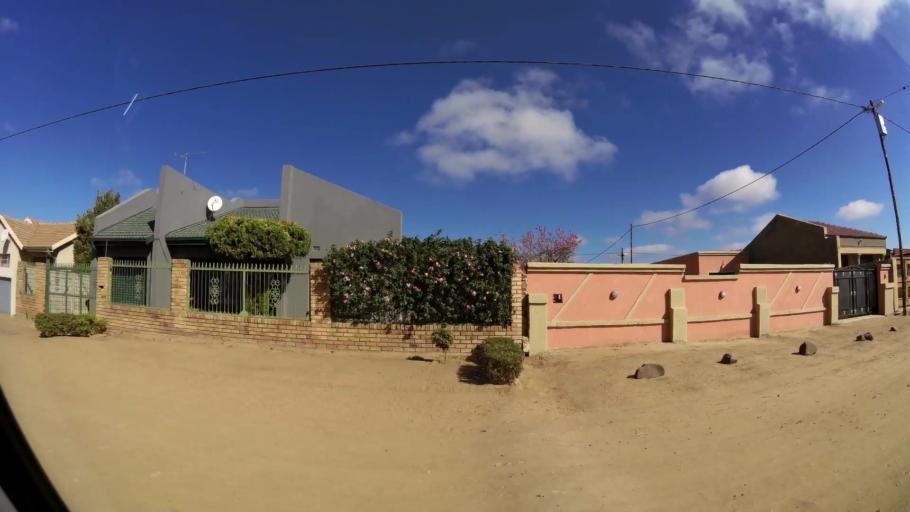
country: ZA
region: Limpopo
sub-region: Capricorn District Municipality
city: Polokwane
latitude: -23.8571
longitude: 29.3804
